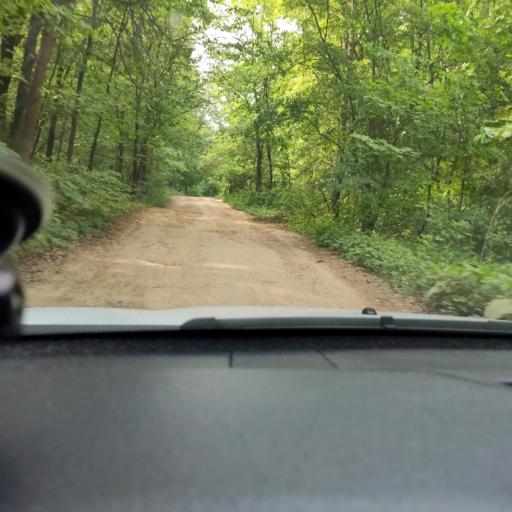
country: RU
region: Samara
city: Novosemeykino
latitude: 53.3367
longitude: 50.2238
